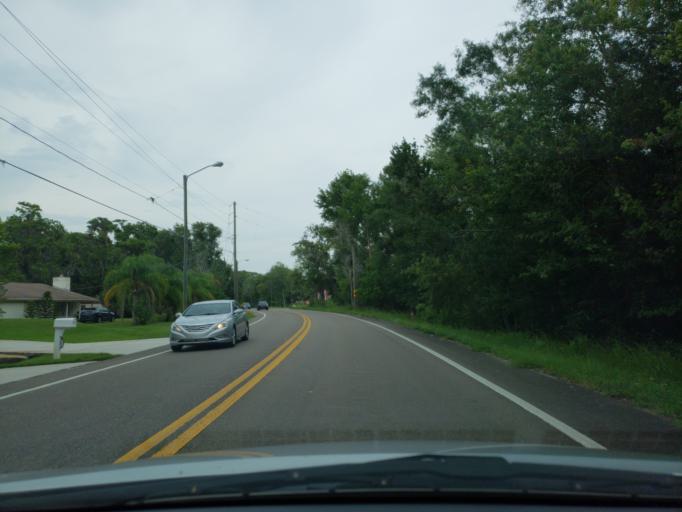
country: US
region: Florida
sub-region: Hillsborough County
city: Cheval
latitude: 28.1549
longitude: -82.4899
